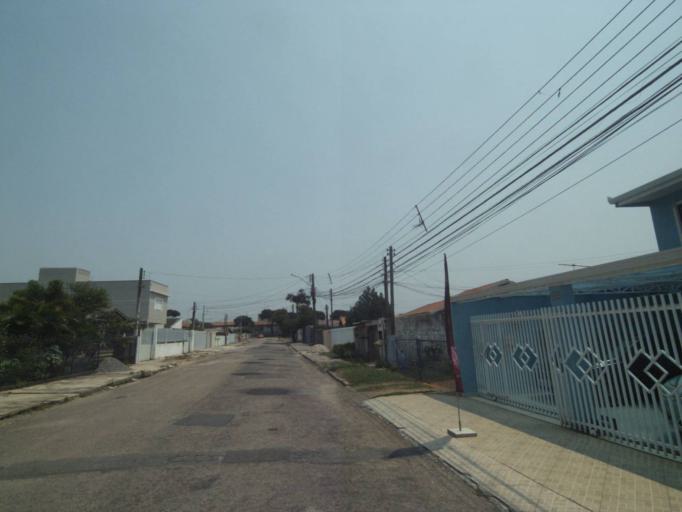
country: BR
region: Parana
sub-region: Sao Jose Dos Pinhais
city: Sao Jose dos Pinhais
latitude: -25.5286
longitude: -49.2389
